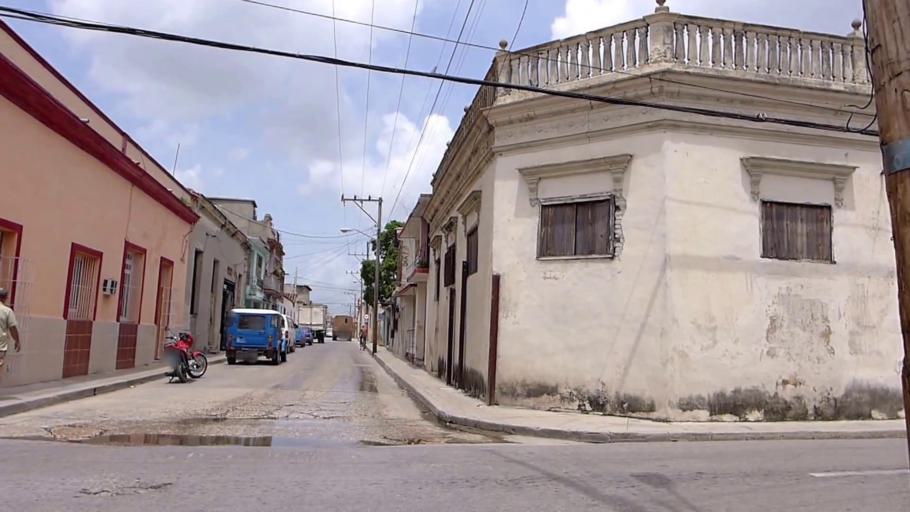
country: CU
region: Holguin
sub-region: Municipio de Holguin
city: Holguin
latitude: 20.8909
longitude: -76.2607
